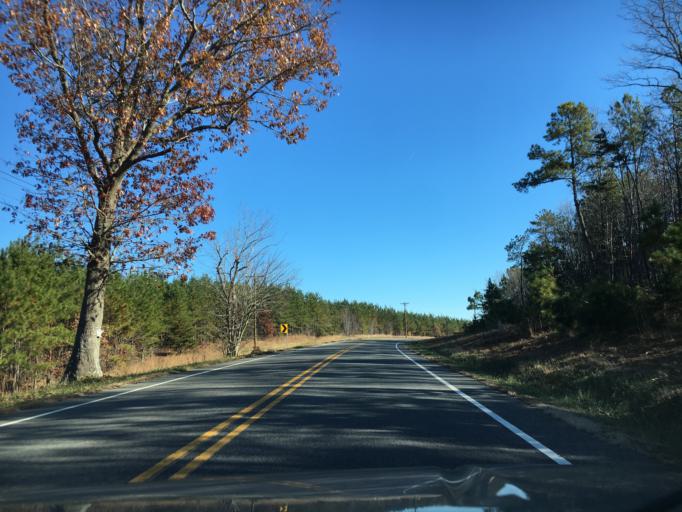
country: US
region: Virginia
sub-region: Appomattox County
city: Appomattox
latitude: 37.4560
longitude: -78.7112
